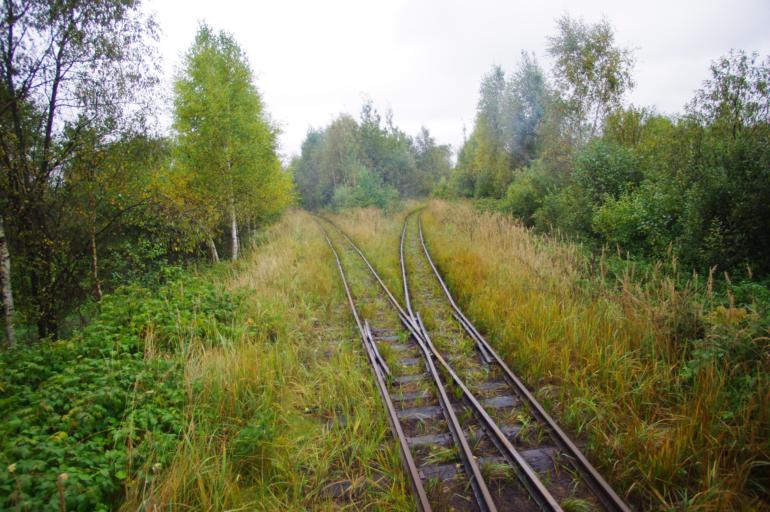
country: RU
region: Vladimir
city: Mezinovskiy
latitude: 55.4847
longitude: 40.4133
